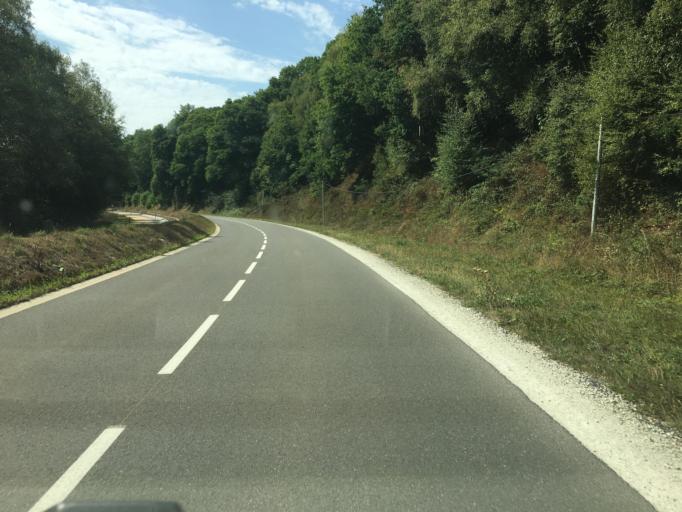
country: FR
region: Brittany
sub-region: Departement des Cotes-d'Armor
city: Gouarec
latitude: 48.2204
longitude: -3.1614
